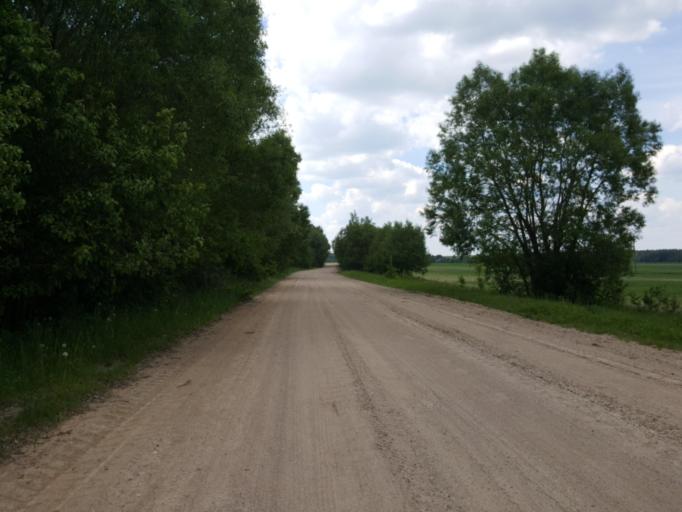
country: BY
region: Brest
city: Kamyanyuki
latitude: 52.5228
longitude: 23.6684
